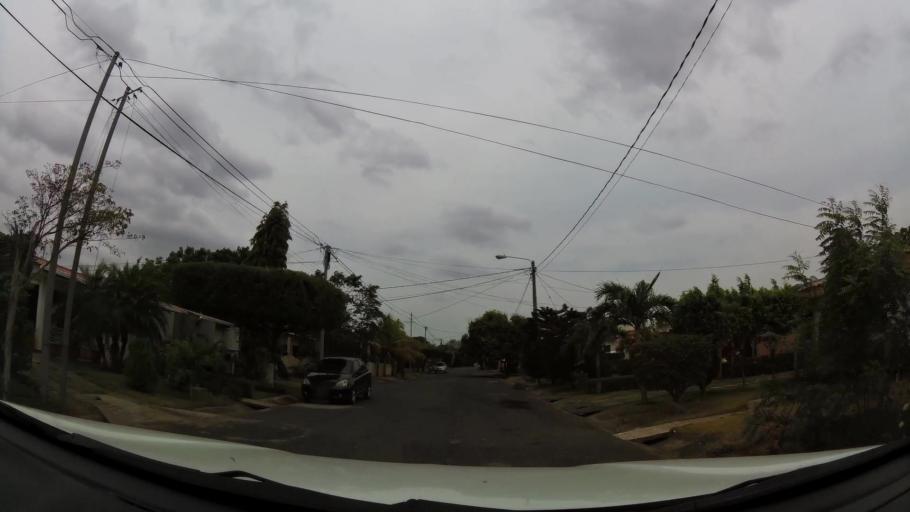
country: NI
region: Masaya
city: Ticuantepe
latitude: 12.0756
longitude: -86.1747
